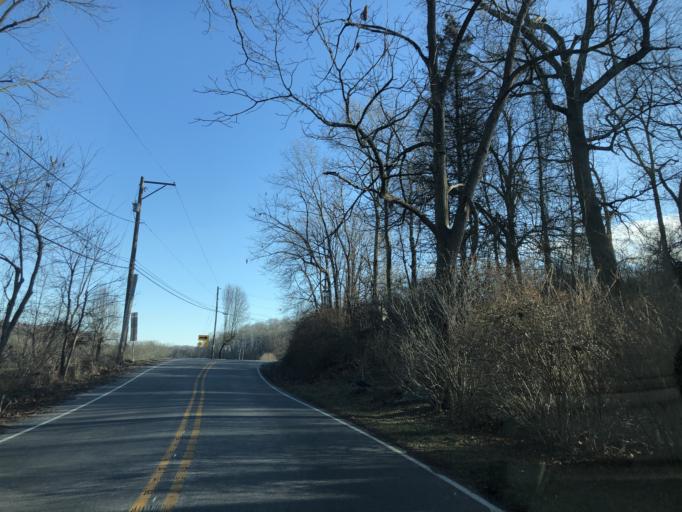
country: US
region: Pennsylvania
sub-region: Chester County
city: South Coatesville
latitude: 39.9317
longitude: -75.8296
